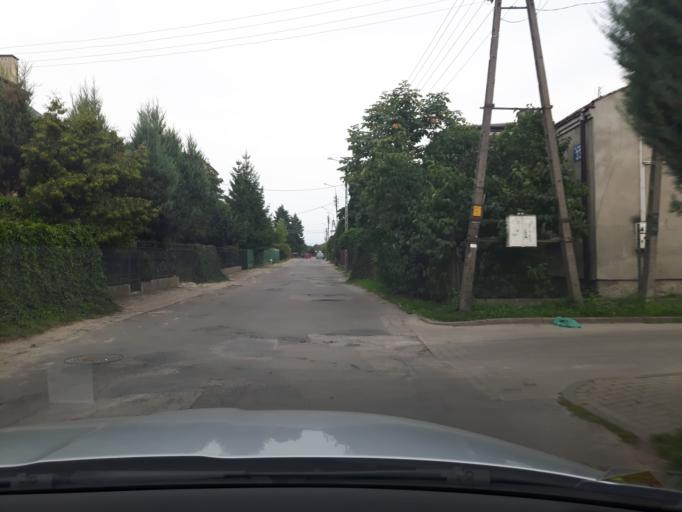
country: PL
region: Masovian Voivodeship
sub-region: Powiat wolominski
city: Zabki
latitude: 52.2944
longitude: 21.1066
